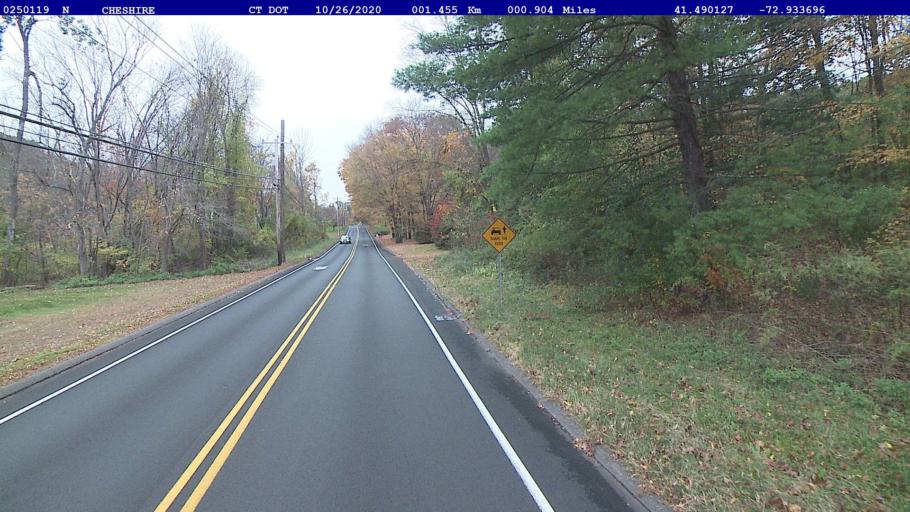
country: US
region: Connecticut
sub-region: New Haven County
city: Cheshire
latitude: 41.4901
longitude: -72.9337
